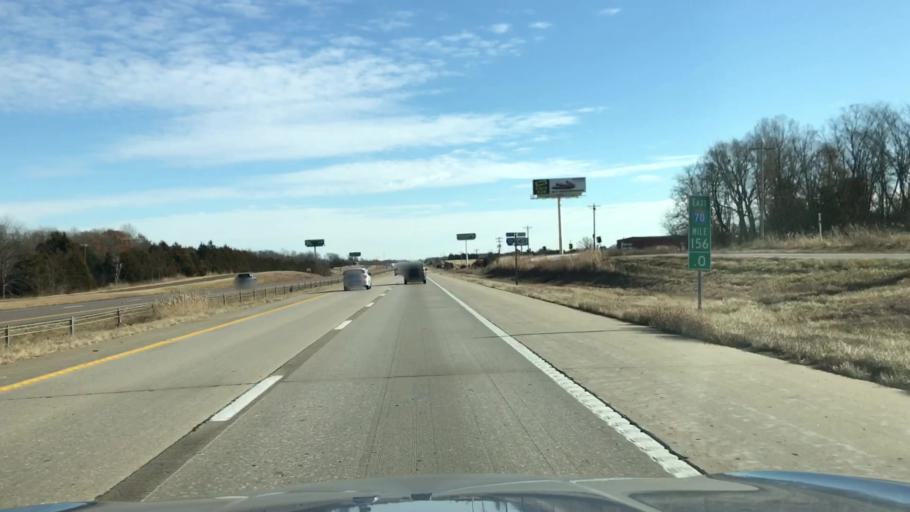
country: US
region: Missouri
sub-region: Callaway County
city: Fulton
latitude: 38.9312
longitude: -91.7969
